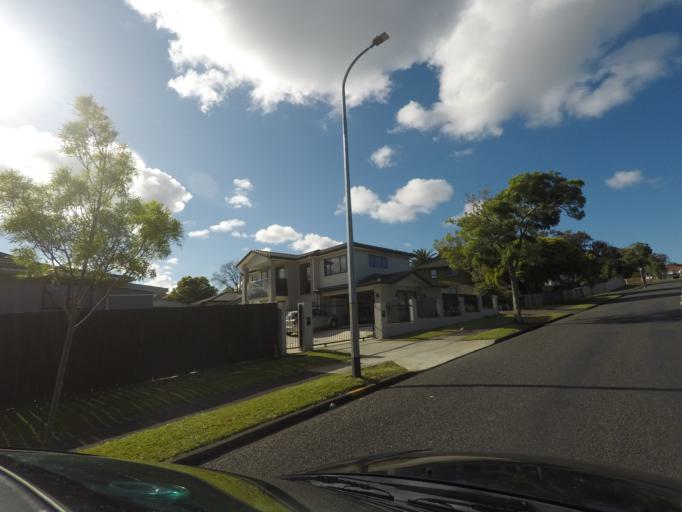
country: NZ
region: Auckland
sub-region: Auckland
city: Manukau City
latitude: -36.9870
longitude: 174.8898
